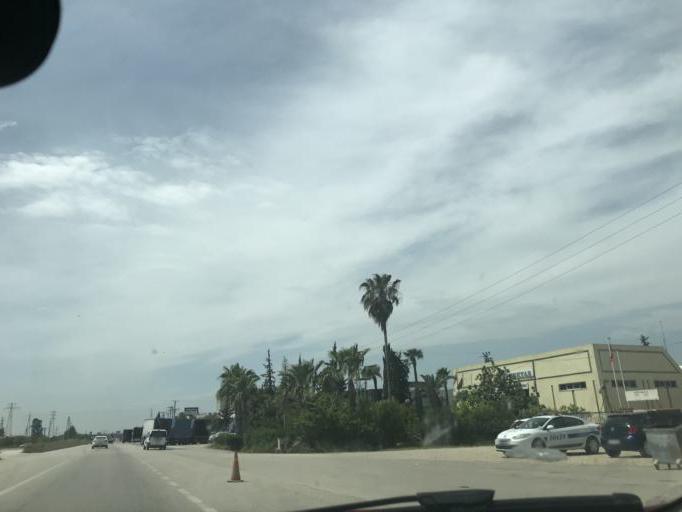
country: TR
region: Adana
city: Yuregir
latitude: 36.9805
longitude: 35.4488
